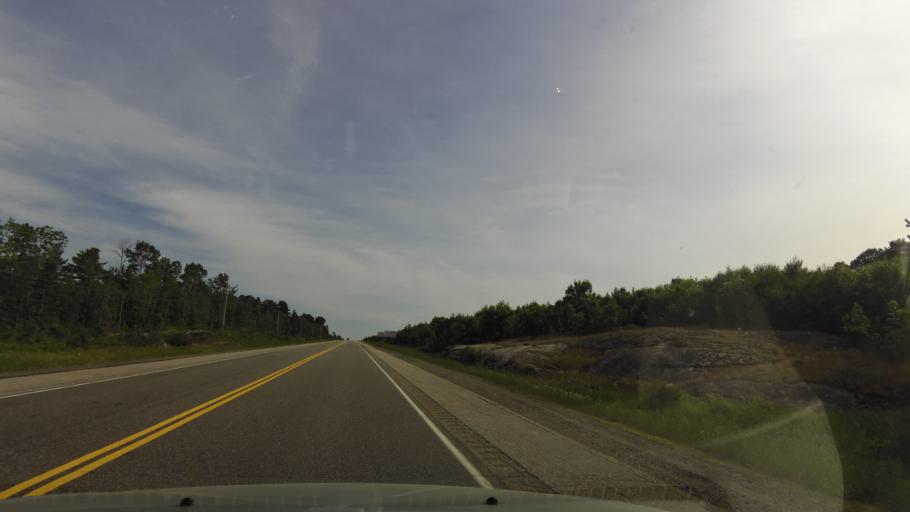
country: CA
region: Ontario
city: Greater Sudbury
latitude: 45.9567
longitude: -80.5804
